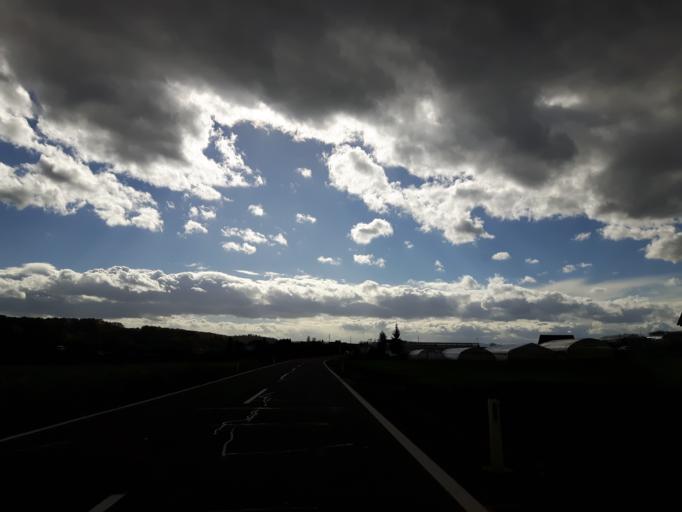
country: AT
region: Styria
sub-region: Politischer Bezirk Leibnitz
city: Wolfsberg im Schwarzautal
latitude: 46.8584
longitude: 15.6496
